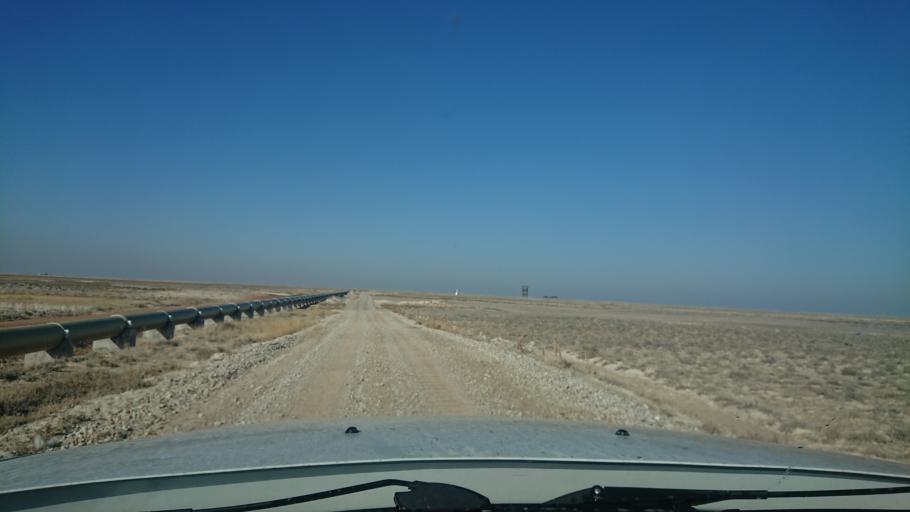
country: TR
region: Aksaray
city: Eskil
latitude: 38.4205
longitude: 33.5021
